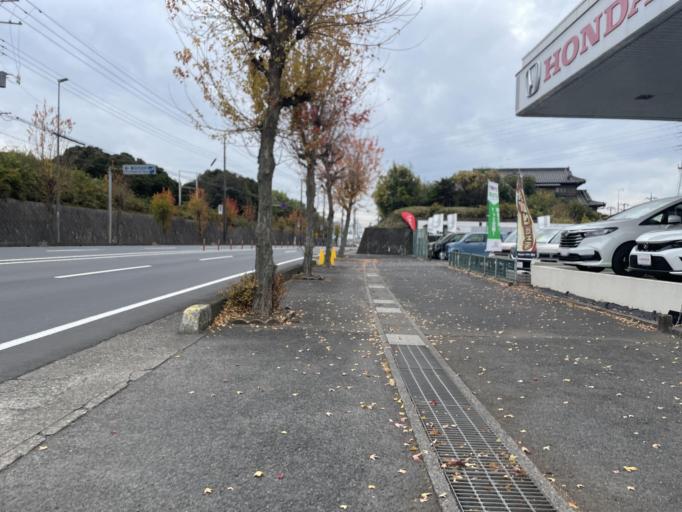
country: JP
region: Saitama
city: Shiraoka
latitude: 35.9998
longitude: 139.6554
